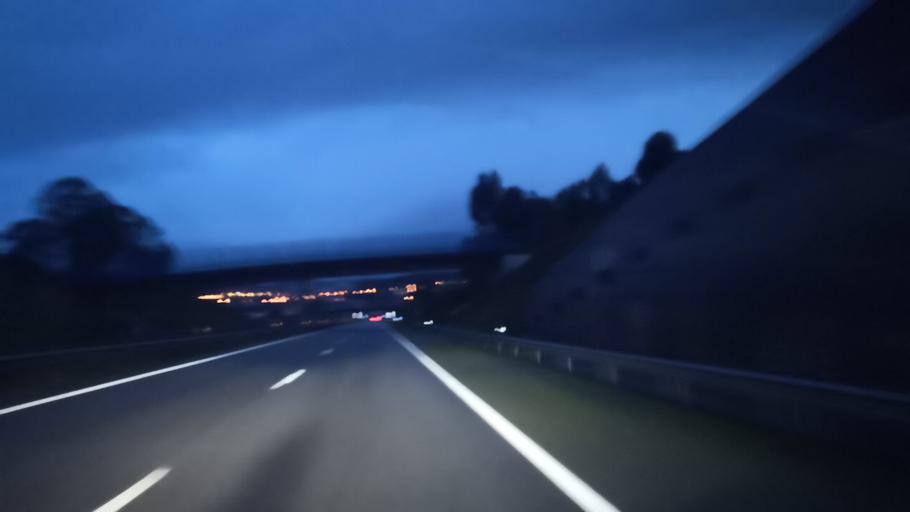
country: PT
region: Braga
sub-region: Braga
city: Oliveira
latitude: 41.4954
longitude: -8.4175
